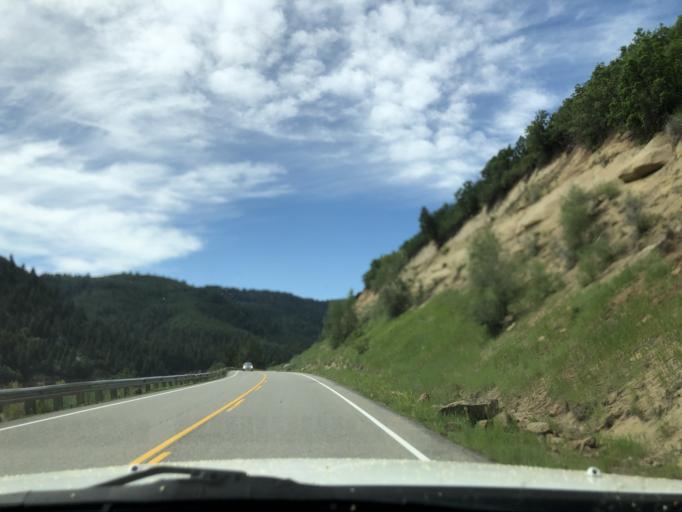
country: US
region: Colorado
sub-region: Delta County
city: Paonia
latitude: 38.9649
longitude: -107.3386
